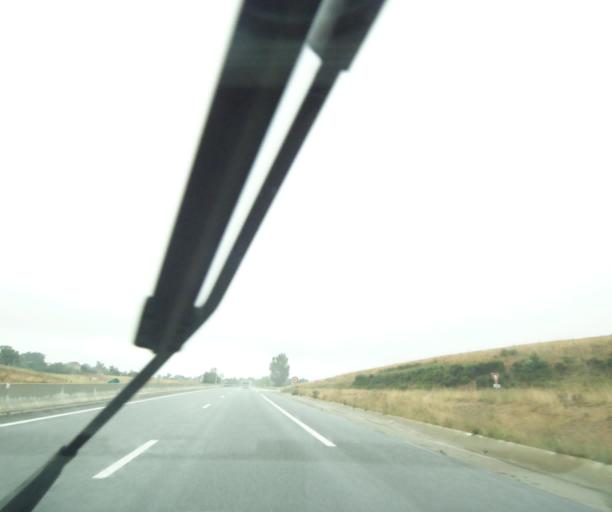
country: FR
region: Midi-Pyrenees
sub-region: Departement de l'Aveyron
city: Naucelle
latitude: 44.1006
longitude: 2.3047
